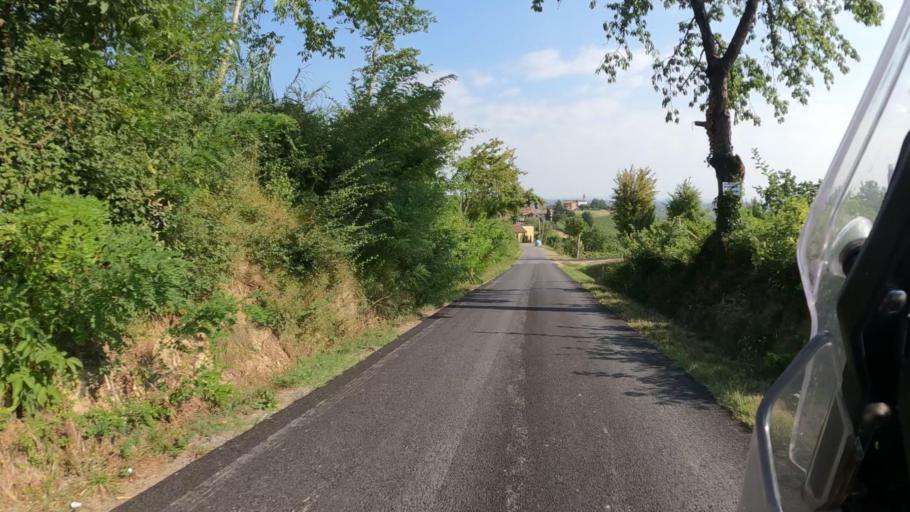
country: IT
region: Piedmont
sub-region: Provincia di Asti
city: Castel Boglione
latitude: 44.7528
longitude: 8.3827
